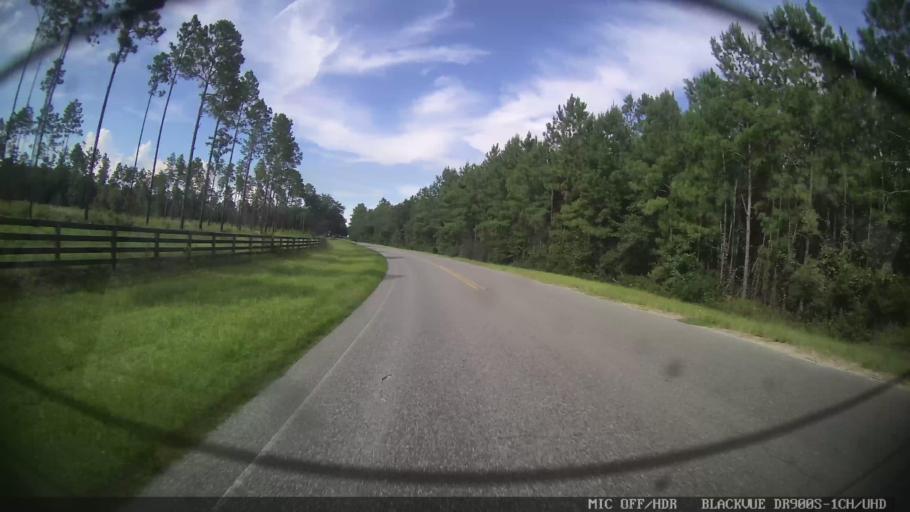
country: US
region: Georgia
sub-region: Echols County
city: Statenville
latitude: 30.6257
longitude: -83.1991
